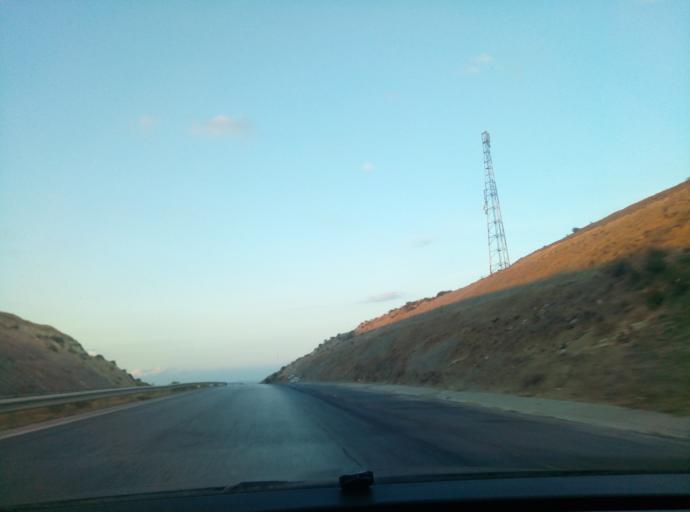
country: TN
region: Manouba
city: Manouba
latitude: 36.7599
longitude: 10.0600
